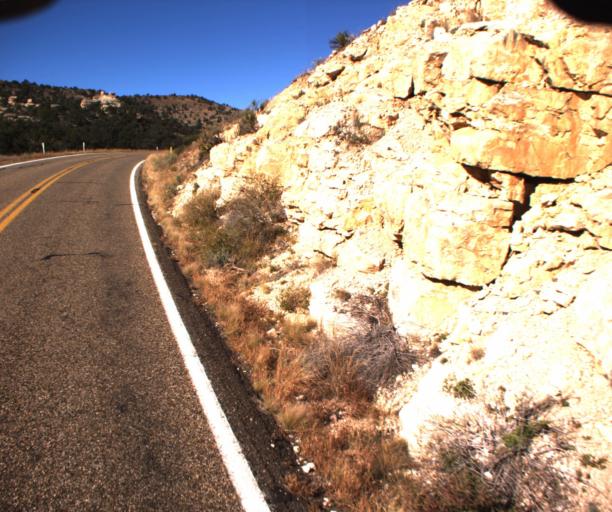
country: US
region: Arizona
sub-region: Coconino County
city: Fredonia
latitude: 36.7252
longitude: -112.0718
